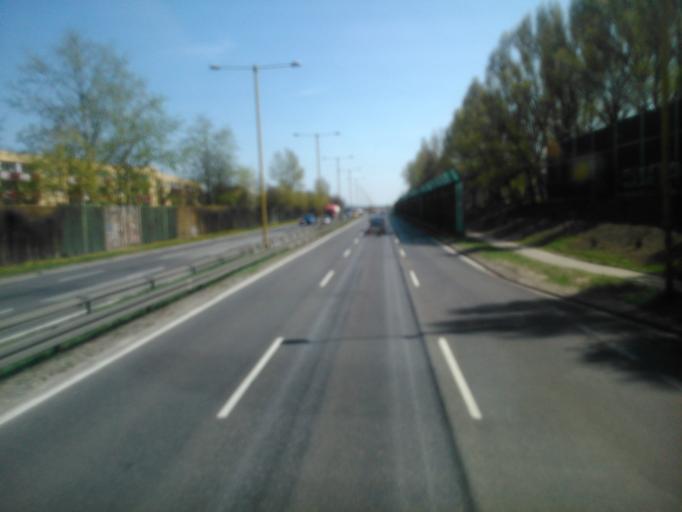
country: PL
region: Silesian Voivodeship
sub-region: Czestochowa
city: Czestochowa
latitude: 50.7755
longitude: 19.1521
